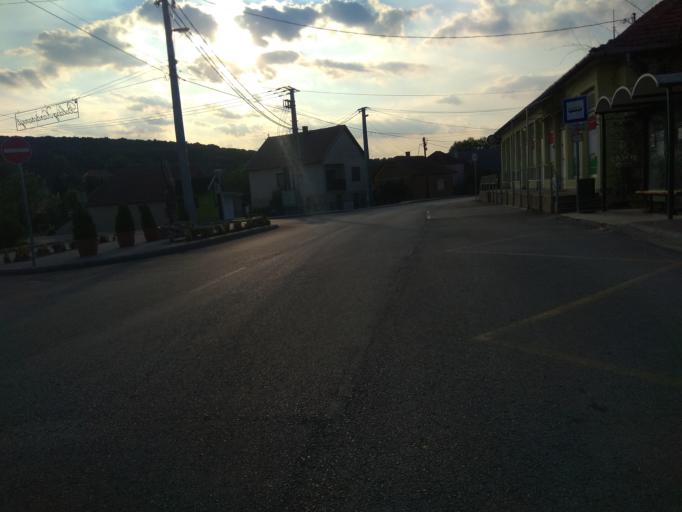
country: HU
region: Borsod-Abauj-Zemplen
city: Harsany
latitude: 47.9852
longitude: 20.7813
